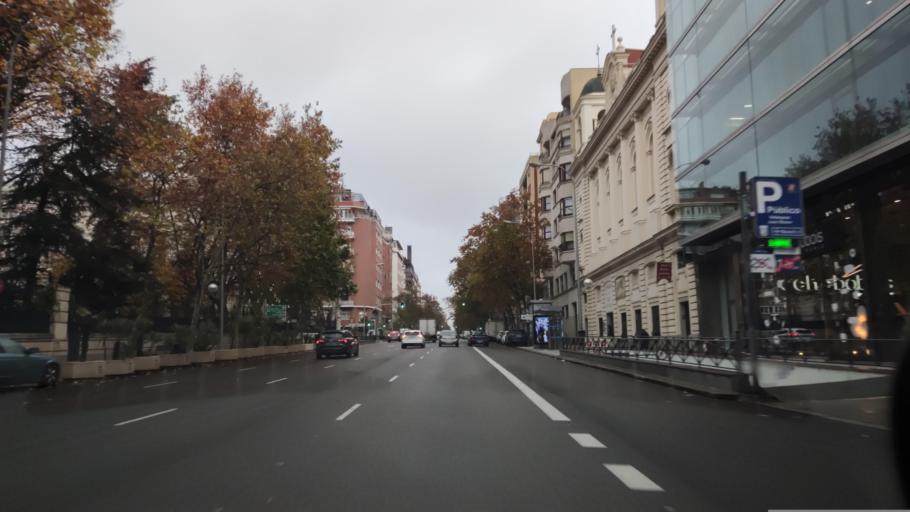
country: ES
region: Madrid
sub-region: Provincia de Madrid
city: Salamanca
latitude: 40.4317
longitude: -3.6835
